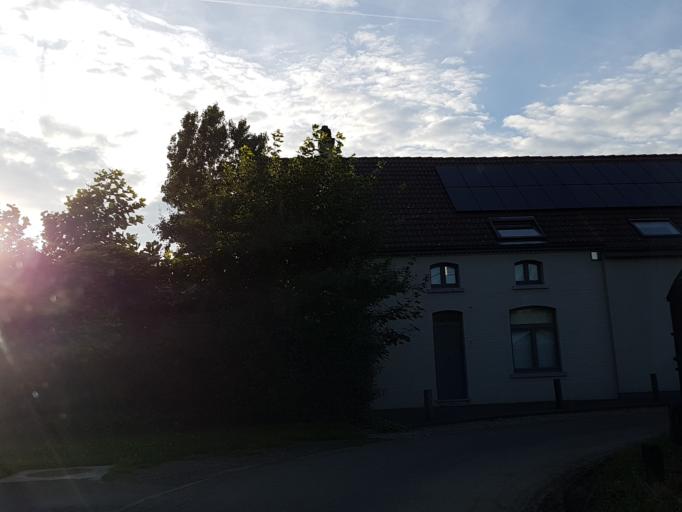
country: BE
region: Flanders
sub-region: Provincie Vlaams-Brabant
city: Merchtem
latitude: 50.9787
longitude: 4.2555
